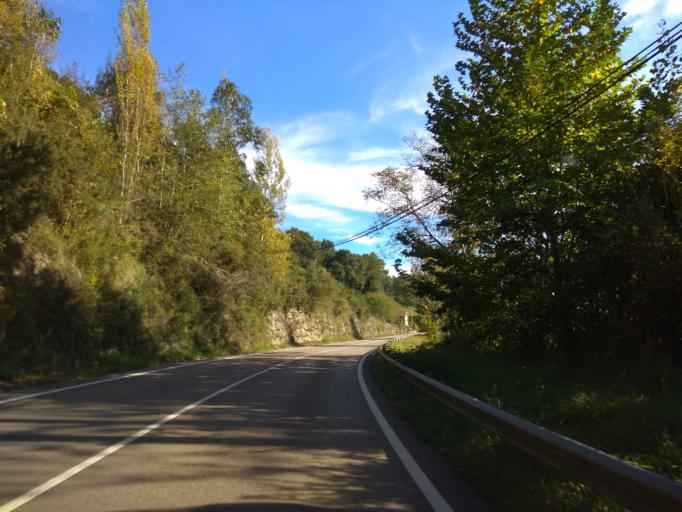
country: ES
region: Cantabria
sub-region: Provincia de Cantabria
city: San Vicente de la Barquera
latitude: 43.3142
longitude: -4.4725
